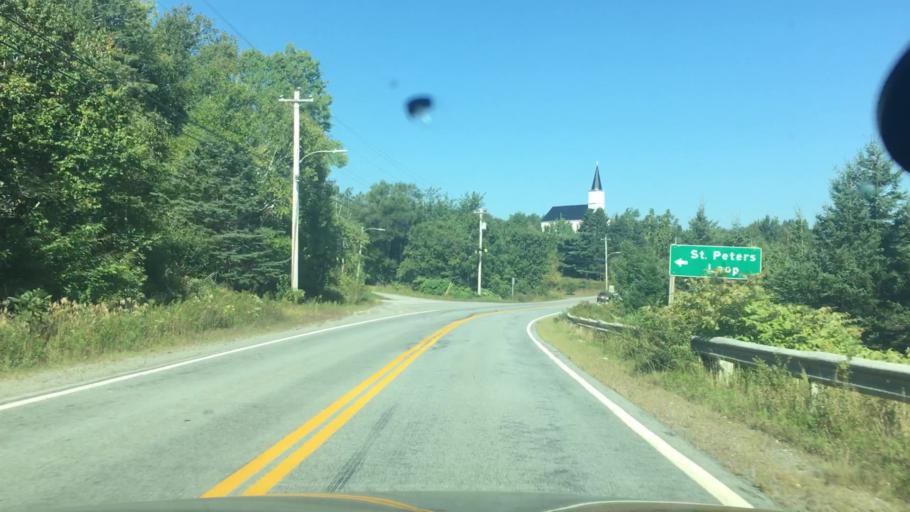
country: CA
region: Nova Scotia
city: New Glasgow
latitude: 44.9218
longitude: -62.5448
